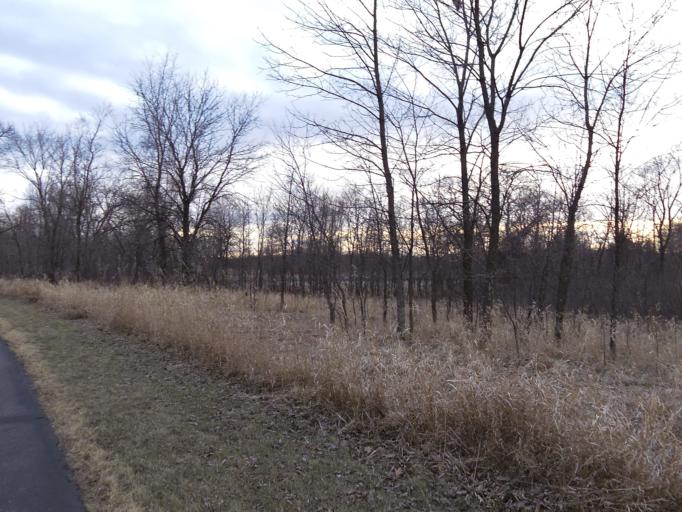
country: US
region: Minnesota
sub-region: Scott County
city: Prior Lake
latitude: 44.6957
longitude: -93.3997
